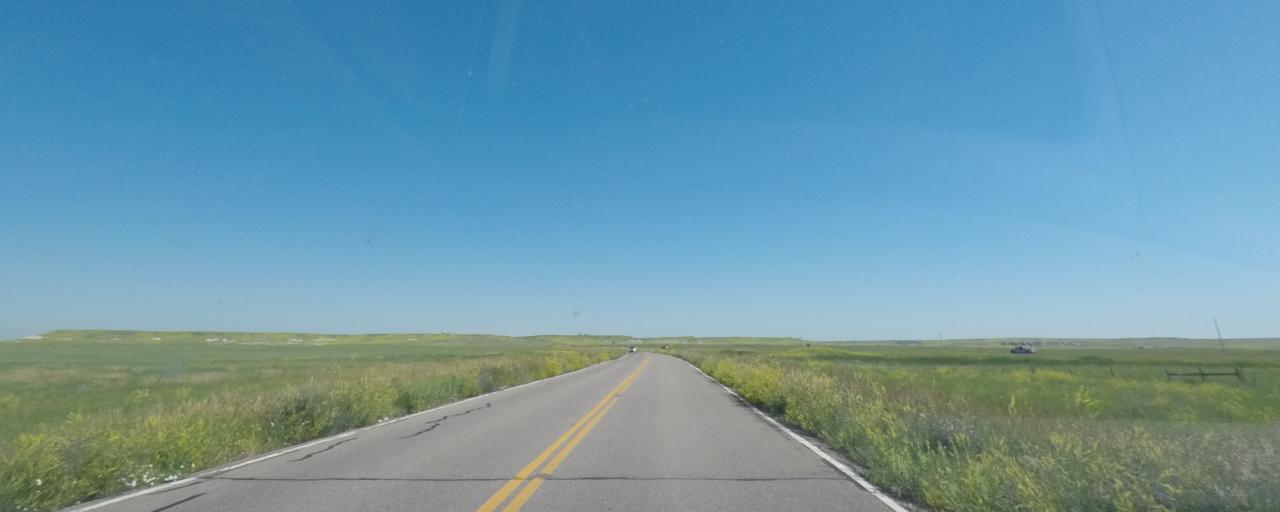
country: US
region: South Dakota
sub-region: Shannon County
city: Porcupine
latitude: 43.7819
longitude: -102.5549
